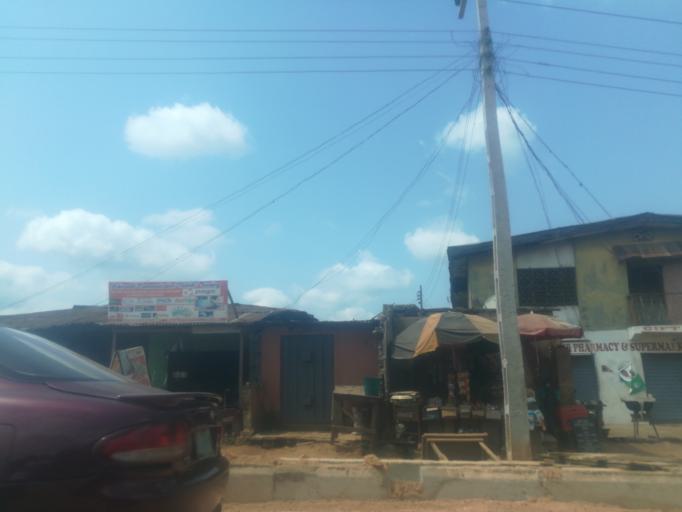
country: NG
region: Oyo
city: Moniya
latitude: 7.5300
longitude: 3.9107
